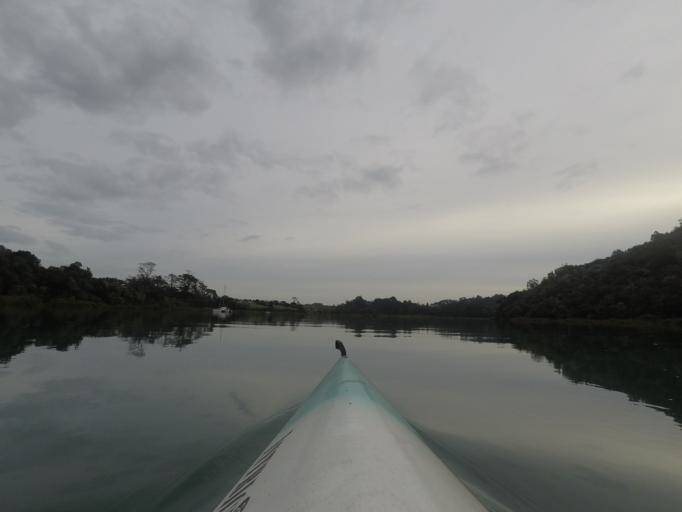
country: NZ
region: Auckland
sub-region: Auckland
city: Rothesay Bay
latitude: -36.6733
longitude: 174.7174
